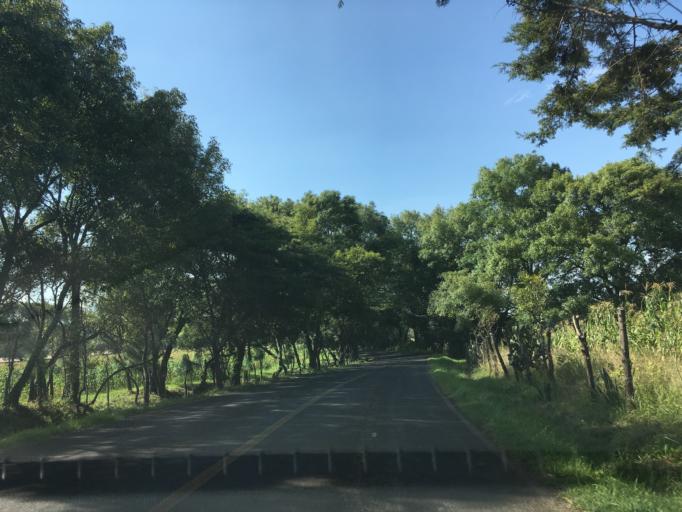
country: MX
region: Michoacan
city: Acuitzio del Canje
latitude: 19.5562
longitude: -101.2704
